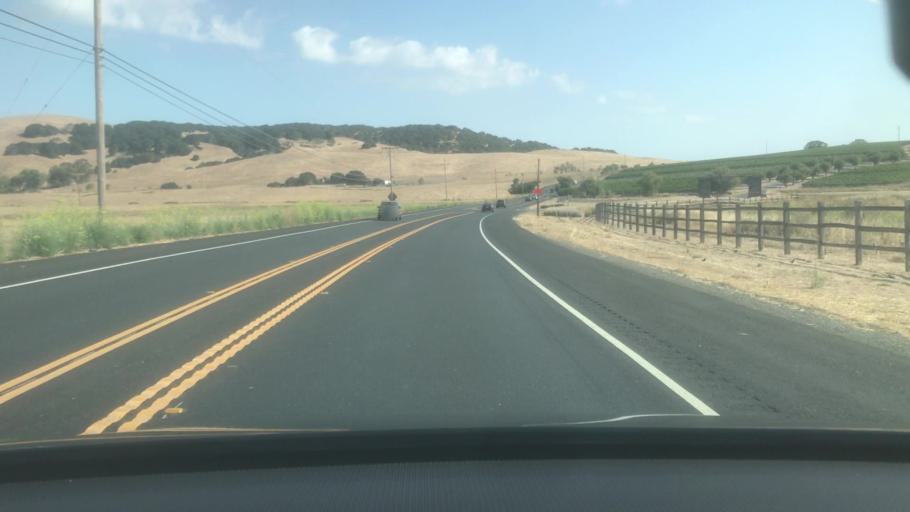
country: US
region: California
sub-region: Marin County
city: Black Point-Green Point
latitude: 38.1716
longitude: -122.4566
